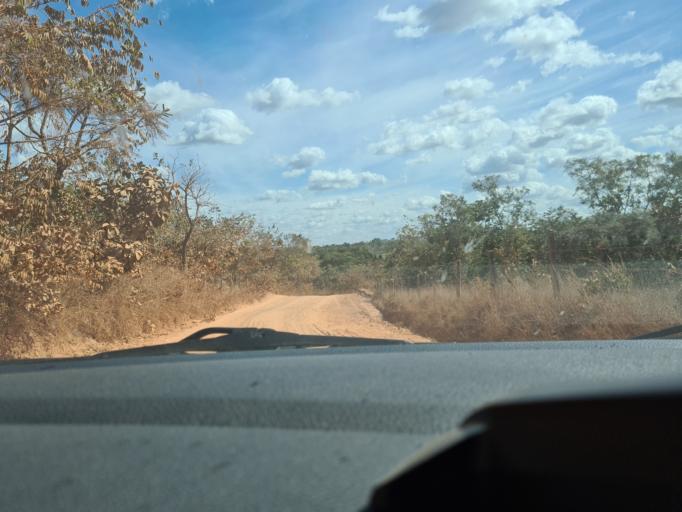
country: BR
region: Goias
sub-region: Silvania
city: Silvania
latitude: -16.5361
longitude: -48.5818
